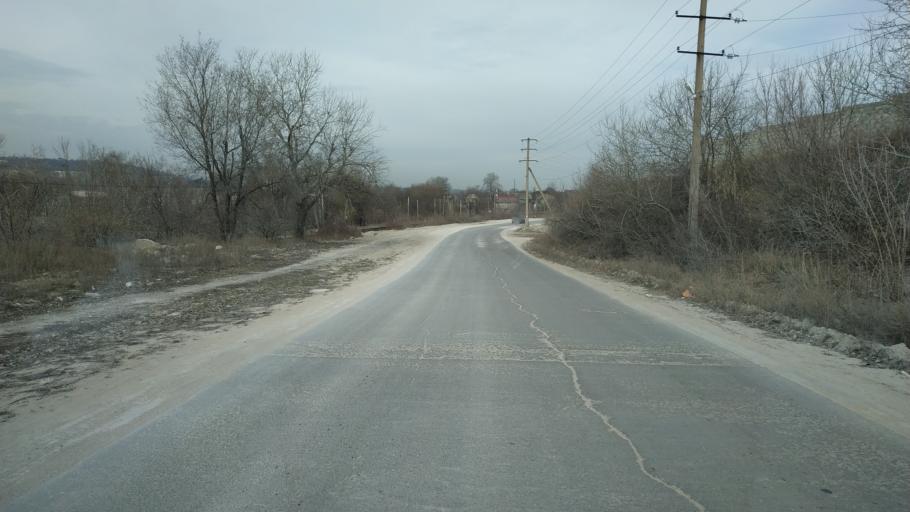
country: MD
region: Chisinau
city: Vatra
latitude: 47.0764
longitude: 28.7436
